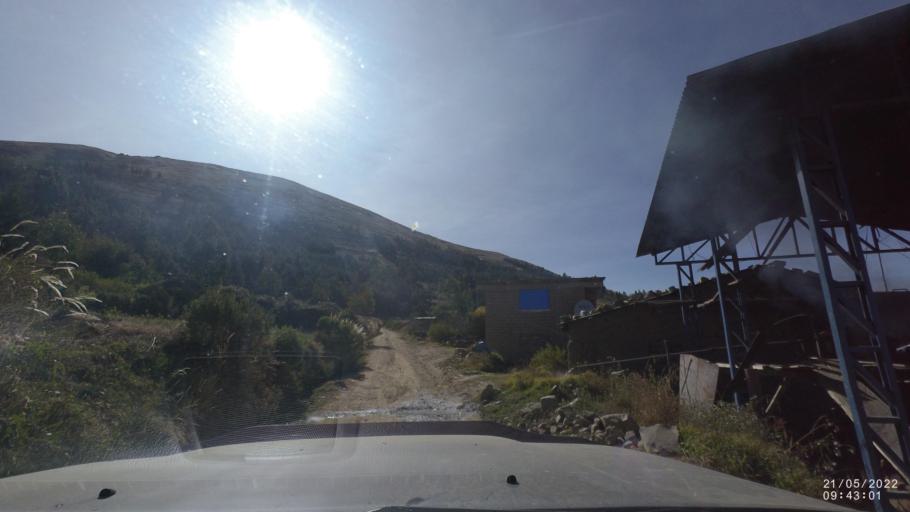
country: BO
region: Cochabamba
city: Colomi
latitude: -17.3404
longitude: -66.0091
